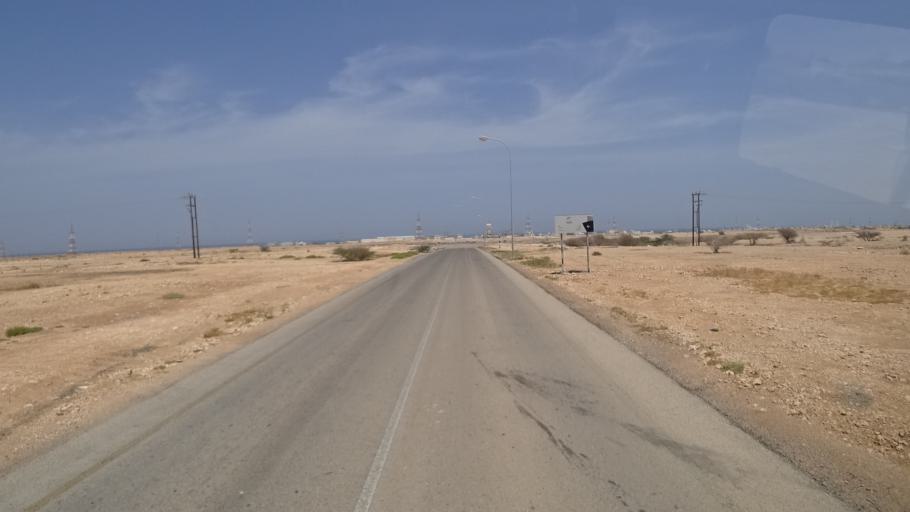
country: OM
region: Ash Sharqiyah
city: Sur
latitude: 22.6138
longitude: 59.4426
